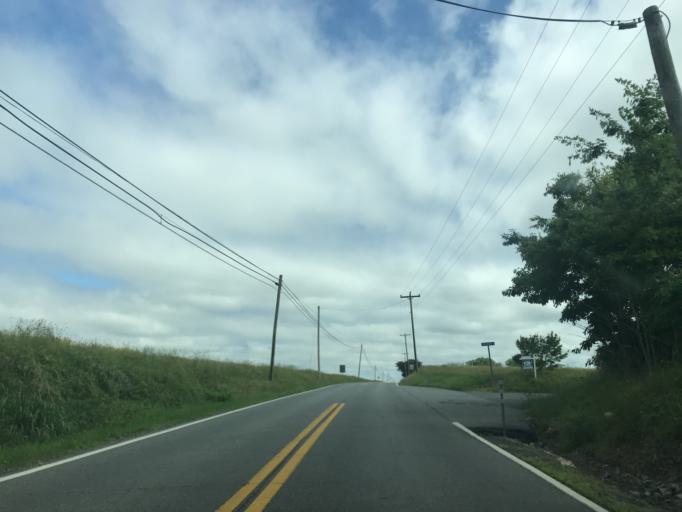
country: US
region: Maryland
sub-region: Caroline County
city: Ridgely
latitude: 38.8924
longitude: -75.9600
